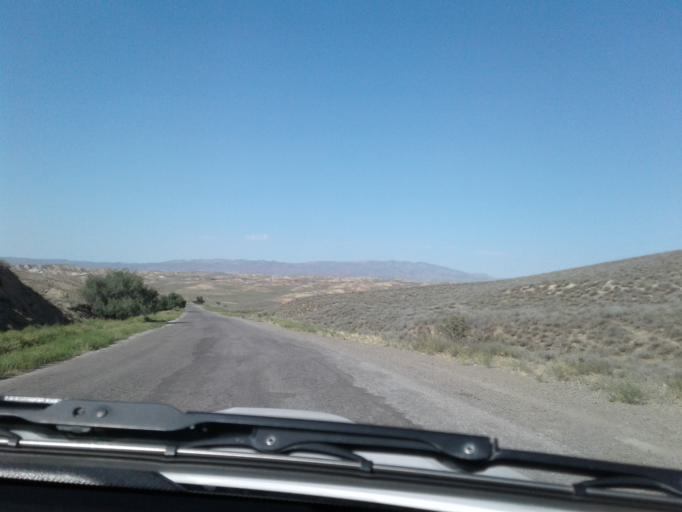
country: TM
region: Balkan
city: Magtymguly
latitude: 38.6556
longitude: 56.2810
